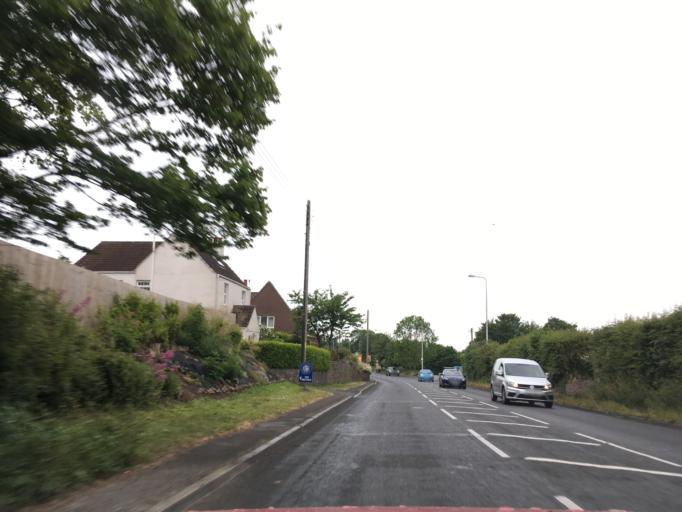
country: GB
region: England
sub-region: North Somerset
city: Brockley
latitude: 51.3945
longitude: -2.7719
